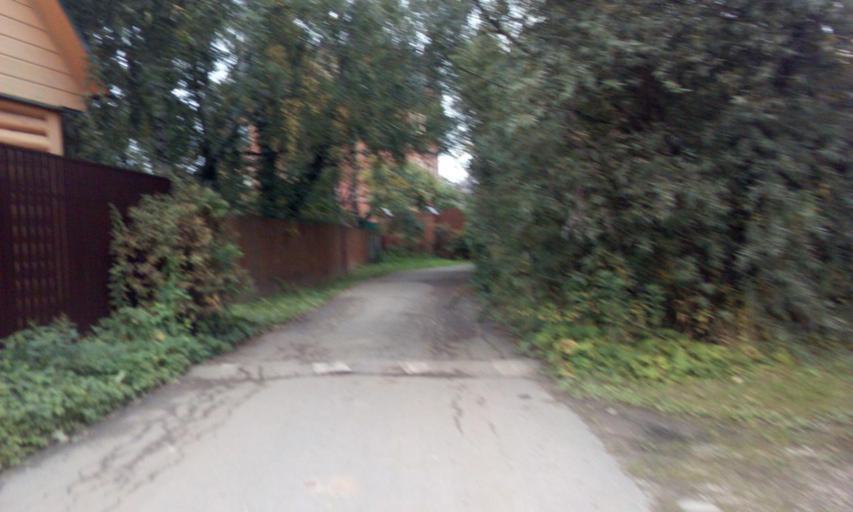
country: RU
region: Moskovskaya
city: Zhavoronki
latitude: 55.6435
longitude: 37.1095
